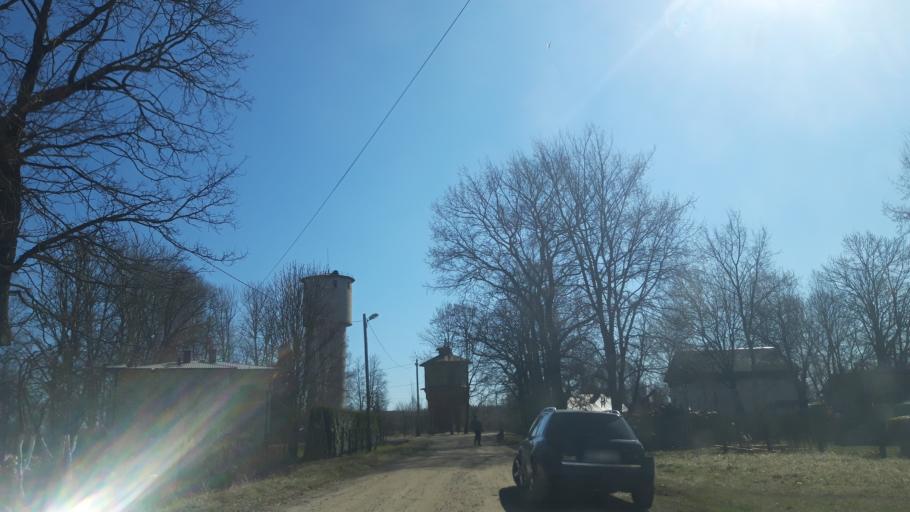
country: LV
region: Valmieras Rajons
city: Valmiera
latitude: 57.5243
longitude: 25.4403
